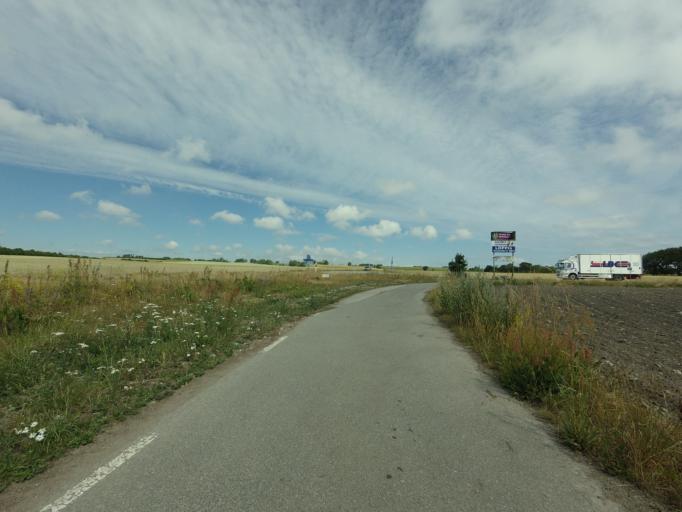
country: SE
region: Skane
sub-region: Simrishamns Kommun
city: Simrishamn
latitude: 55.5108
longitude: 14.3361
